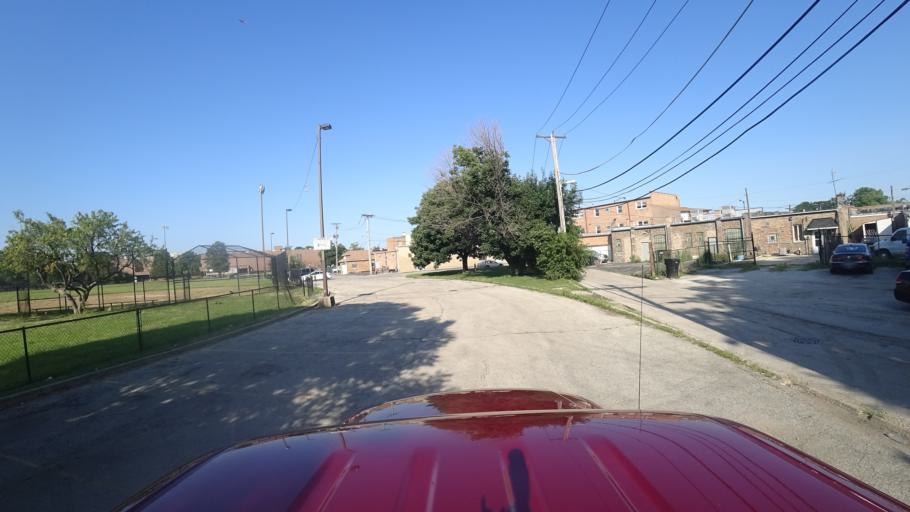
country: US
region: Illinois
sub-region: Cook County
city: Cicero
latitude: 41.8041
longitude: -87.7191
